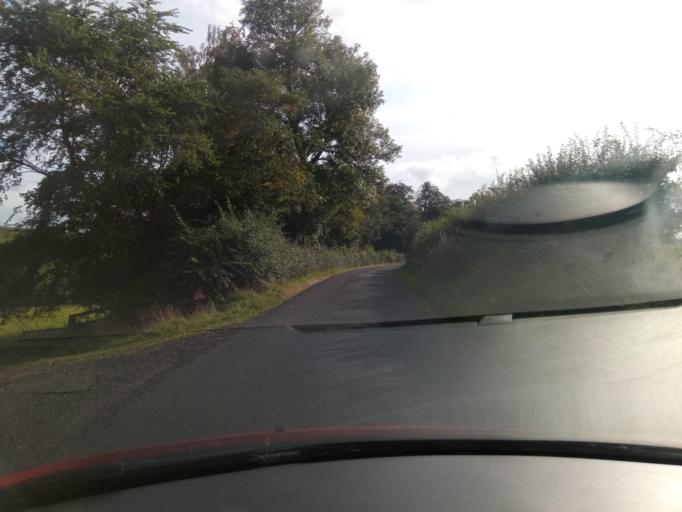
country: GB
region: Scotland
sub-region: The Scottish Borders
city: Kelso
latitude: 55.4868
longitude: -2.3477
